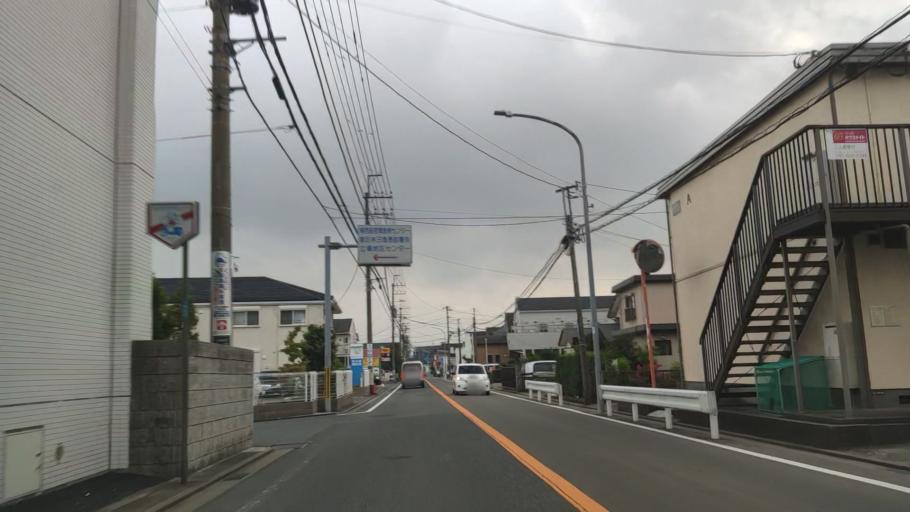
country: JP
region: Kanagawa
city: Fujisawa
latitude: 35.4178
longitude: 139.5002
